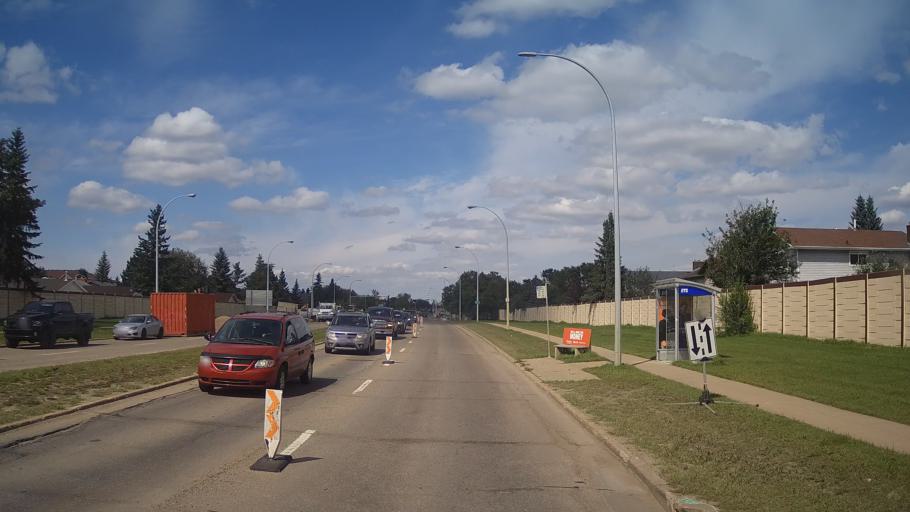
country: CA
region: Alberta
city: St. Albert
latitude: 53.5264
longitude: -113.6299
